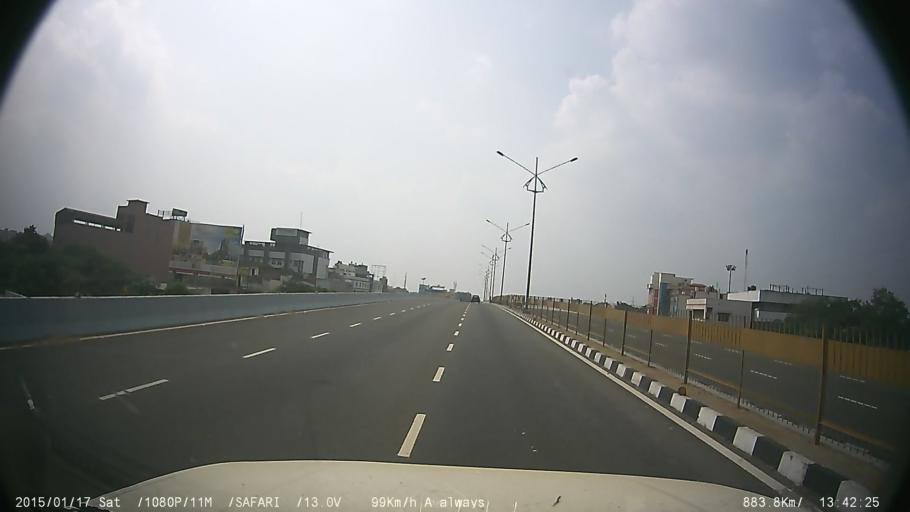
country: IN
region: Tamil Nadu
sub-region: Vellore
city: Vellore
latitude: 12.9328
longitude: 79.1399
